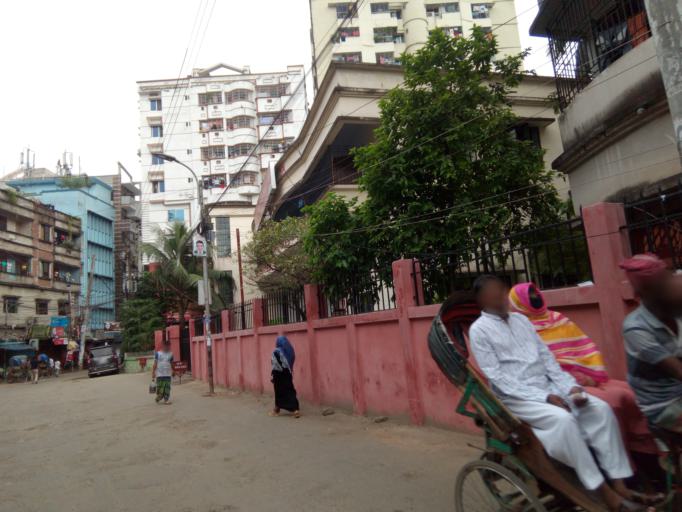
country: BD
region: Dhaka
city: Azimpur
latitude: 23.7220
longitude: 90.3903
